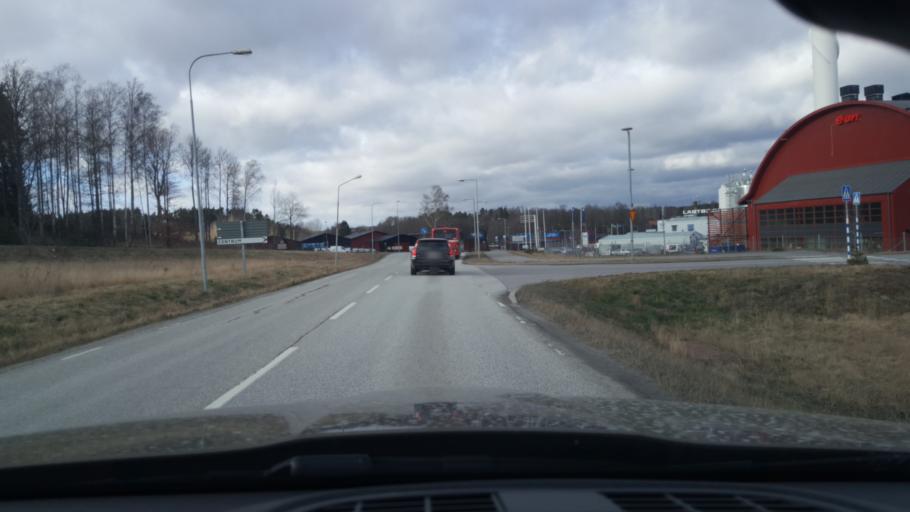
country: SE
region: Stockholm
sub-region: Osterakers Kommun
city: Akersberga
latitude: 59.4901
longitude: 18.2747
